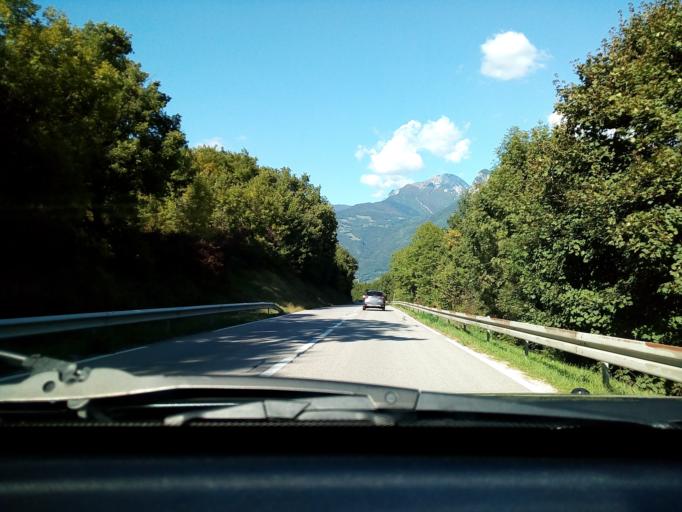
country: FR
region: Rhone-Alpes
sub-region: Departement de l'Isere
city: Sassenage
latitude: 45.2209
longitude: 5.6507
